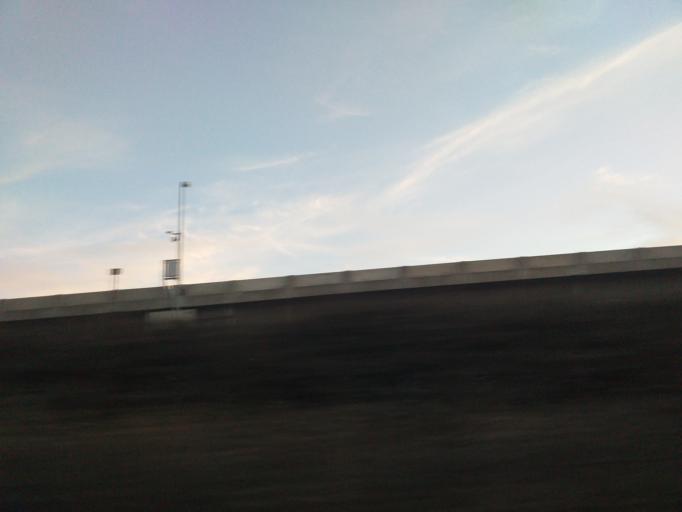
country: TR
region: Ankara
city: Ankara
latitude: 39.9553
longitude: 32.8267
